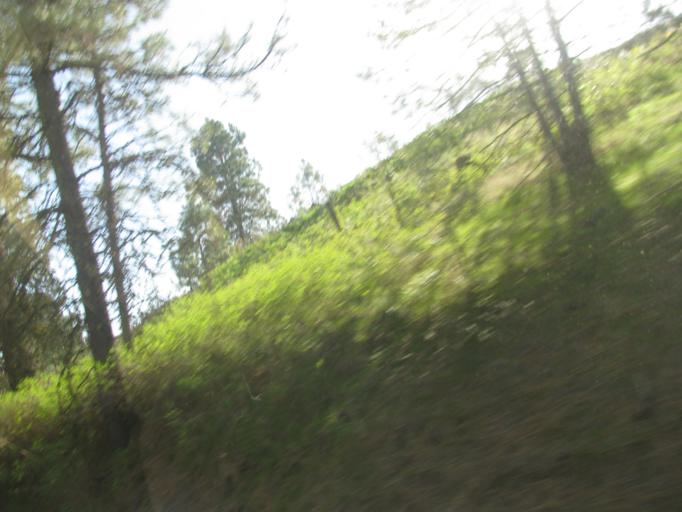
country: US
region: Washington
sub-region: Spokane County
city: Medical Lake
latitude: 47.3581
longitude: -117.8251
